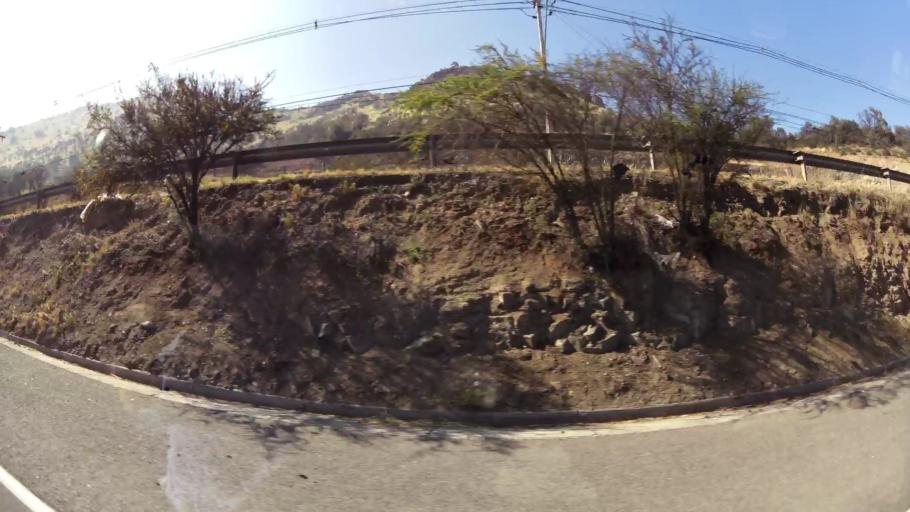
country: CL
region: Santiago Metropolitan
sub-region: Provincia de Chacabuco
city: Chicureo Abajo
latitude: -33.3408
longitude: -70.6932
